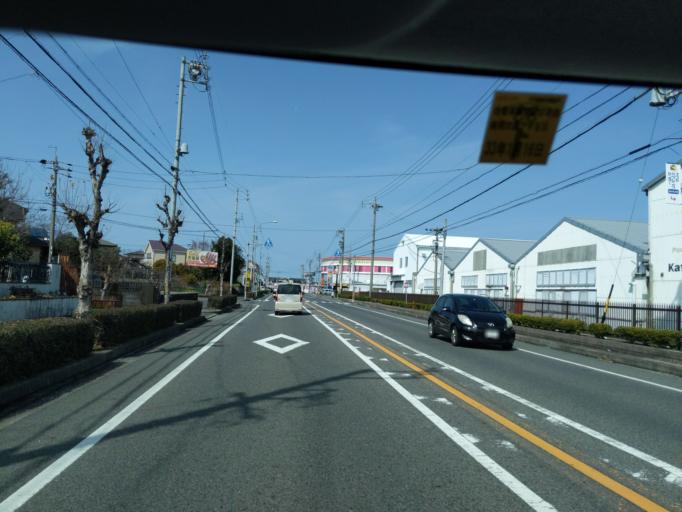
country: JP
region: Aichi
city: Kasugai
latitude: 35.2683
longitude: 136.9602
